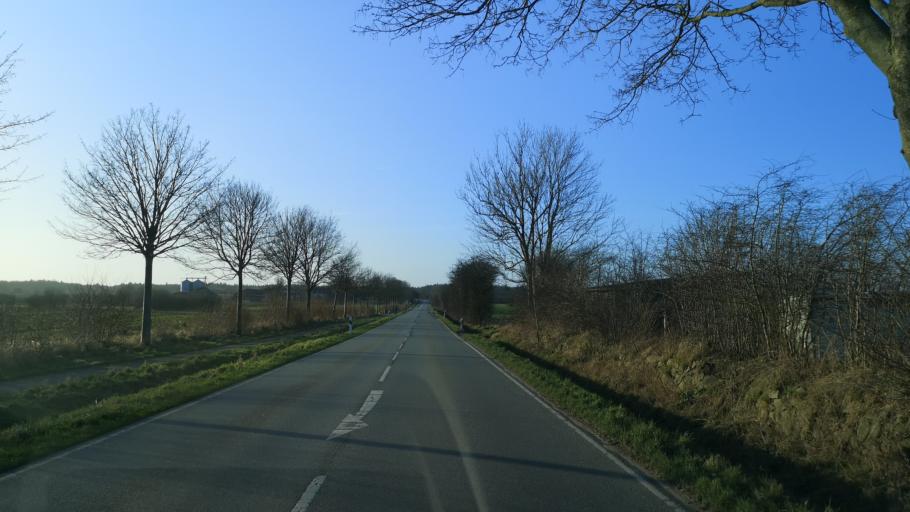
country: DE
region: Schleswig-Holstein
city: Satrup
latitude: 54.6950
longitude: 9.5851
